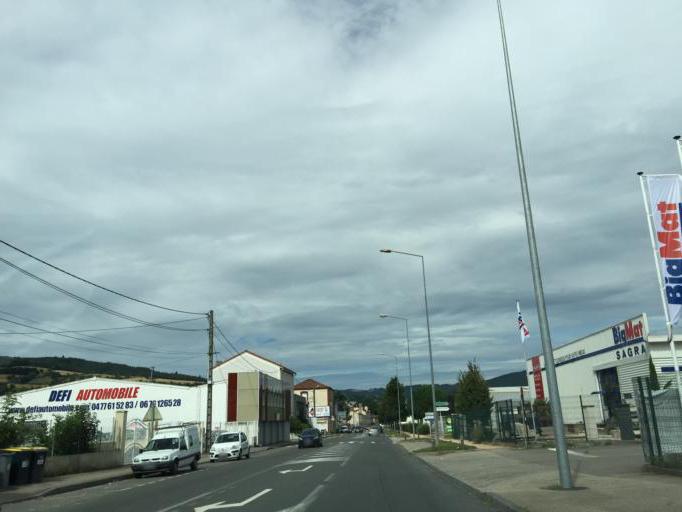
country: FR
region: Rhone-Alpes
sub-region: Departement de la Loire
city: Unieux
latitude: 45.3904
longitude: 4.2799
